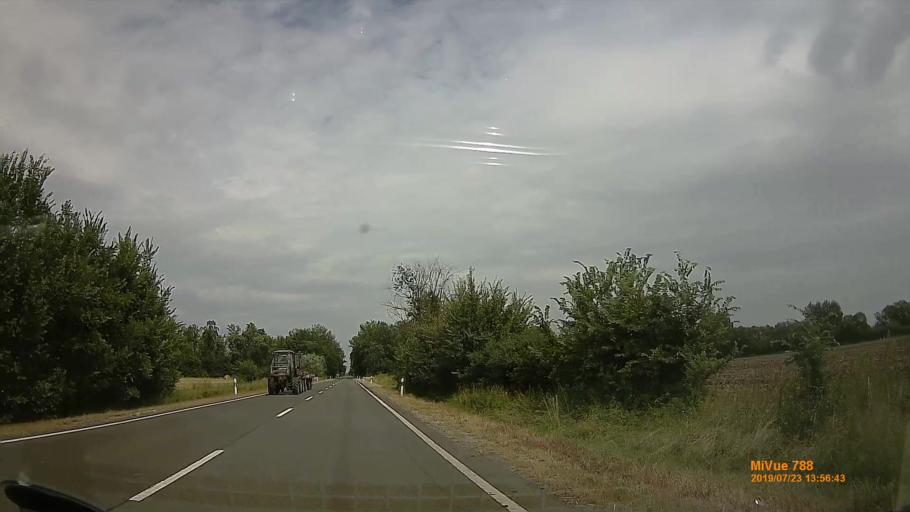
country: HU
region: Hajdu-Bihar
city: Gorbehaza
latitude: 47.9275
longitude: 21.2408
